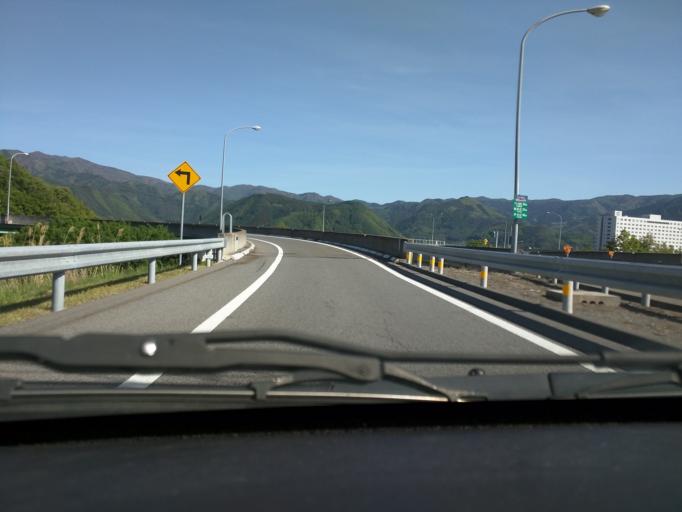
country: JP
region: Nagano
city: Nagano-shi
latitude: 36.5763
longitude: 138.2002
